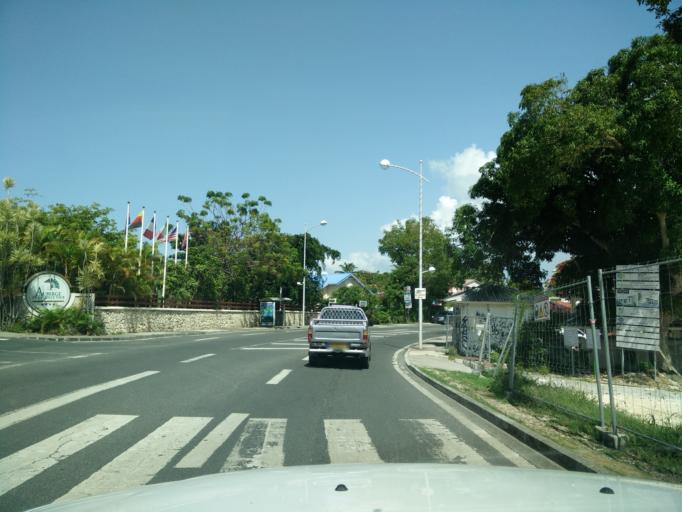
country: GP
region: Guadeloupe
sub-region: Guadeloupe
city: Le Gosier
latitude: 16.2065
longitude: -61.4988
